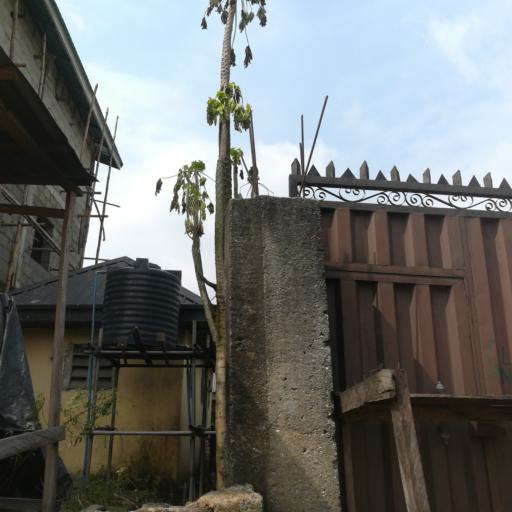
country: NG
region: Rivers
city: Port Harcourt
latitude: 4.8347
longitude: 7.0654
